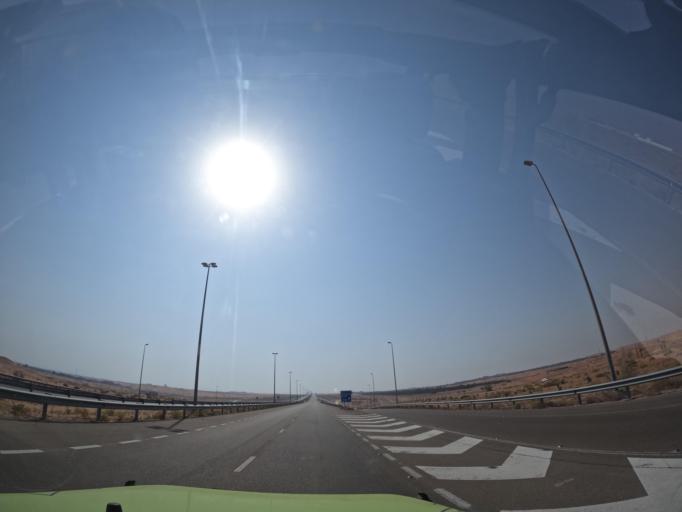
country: OM
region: Al Buraimi
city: Al Buraymi
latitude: 24.4102
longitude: 55.7024
